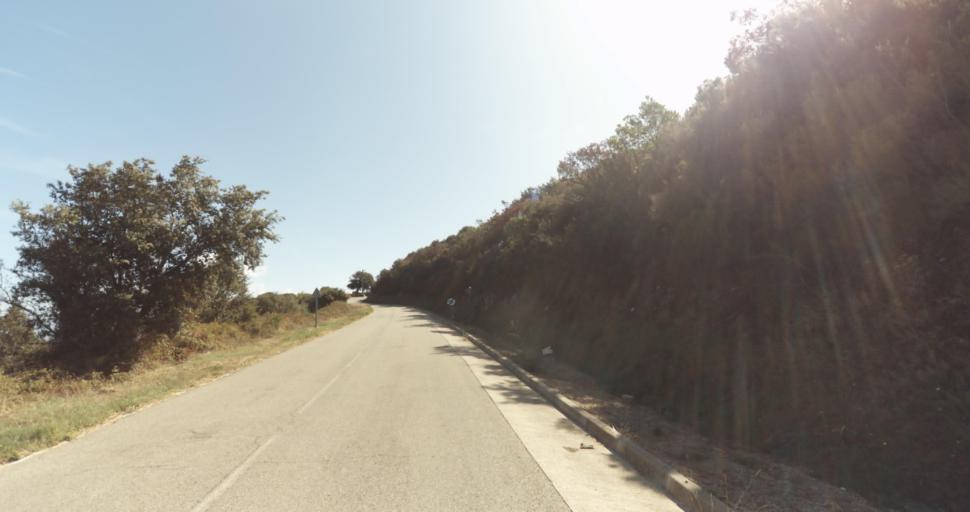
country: FR
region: Corsica
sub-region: Departement de la Corse-du-Sud
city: Ajaccio
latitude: 41.9279
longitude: 8.7046
